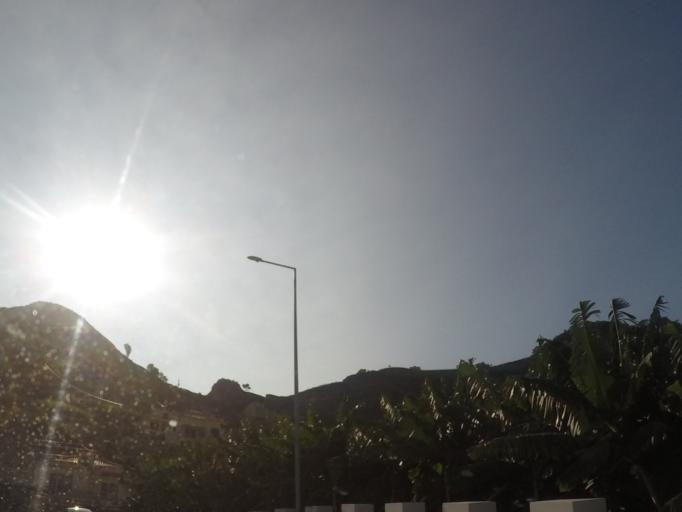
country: PT
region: Madeira
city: Camara de Lobos
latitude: 32.6572
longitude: -16.9917
